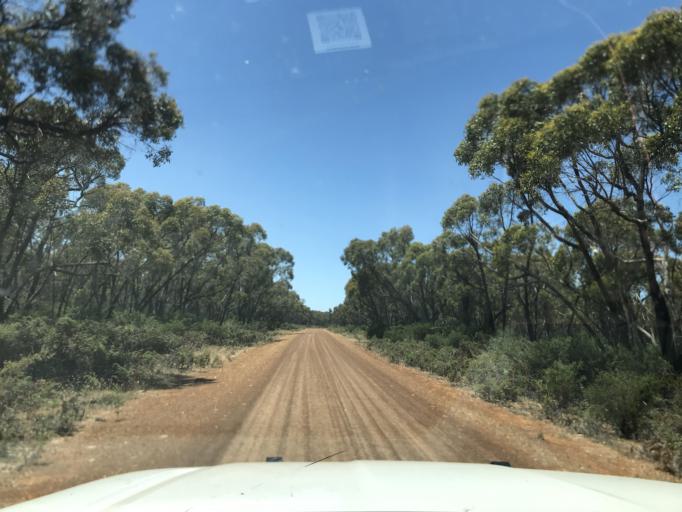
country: AU
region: South Australia
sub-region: Wattle Range
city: Penola
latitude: -37.0463
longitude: 141.3885
